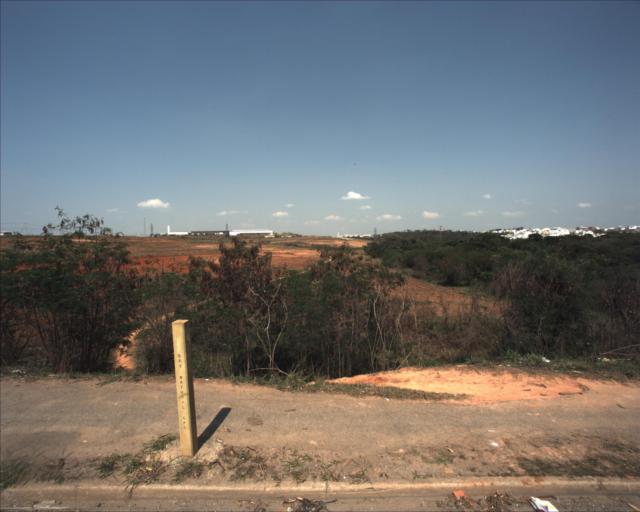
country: BR
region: Sao Paulo
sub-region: Sorocaba
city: Sorocaba
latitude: -23.4307
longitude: -47.4494
